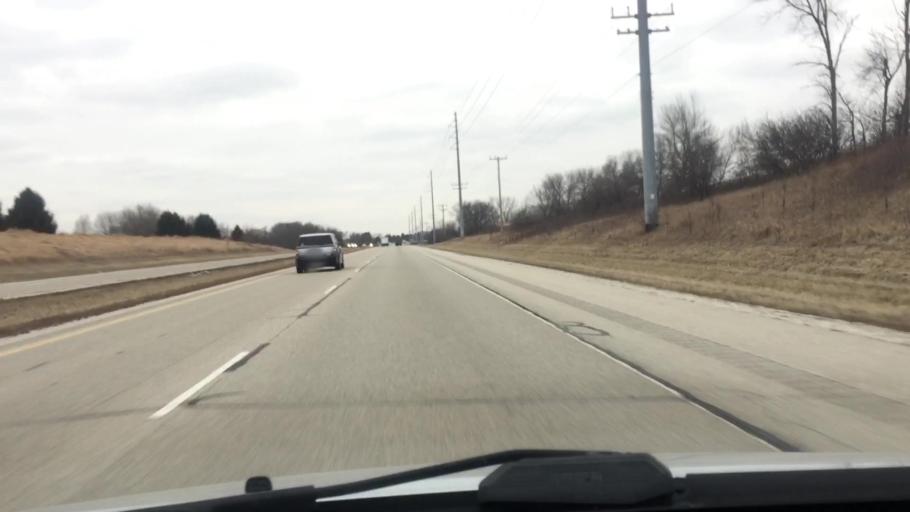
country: US
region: Wisconsin
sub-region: Waukesha County
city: Sussex
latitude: 43.0972
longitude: -88.2066
